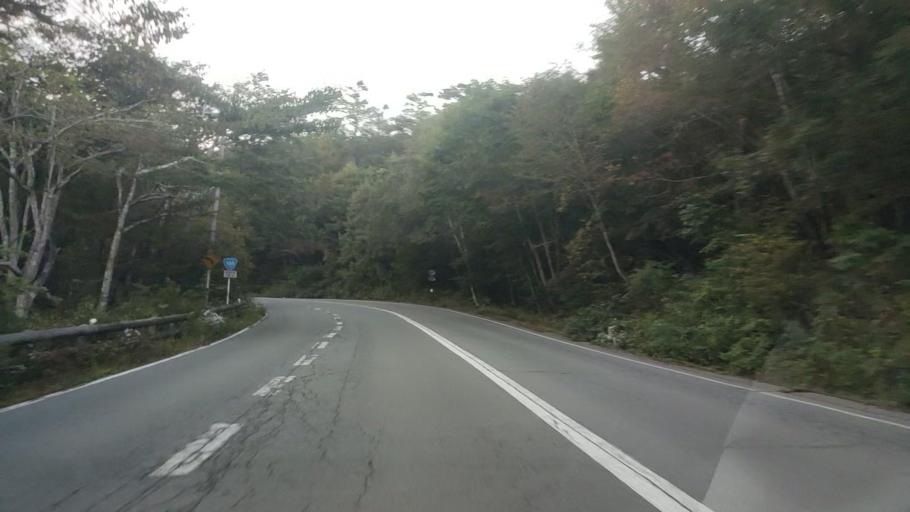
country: JP
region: Nagano
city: Komoro
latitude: 36.3944
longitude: 138.5835
